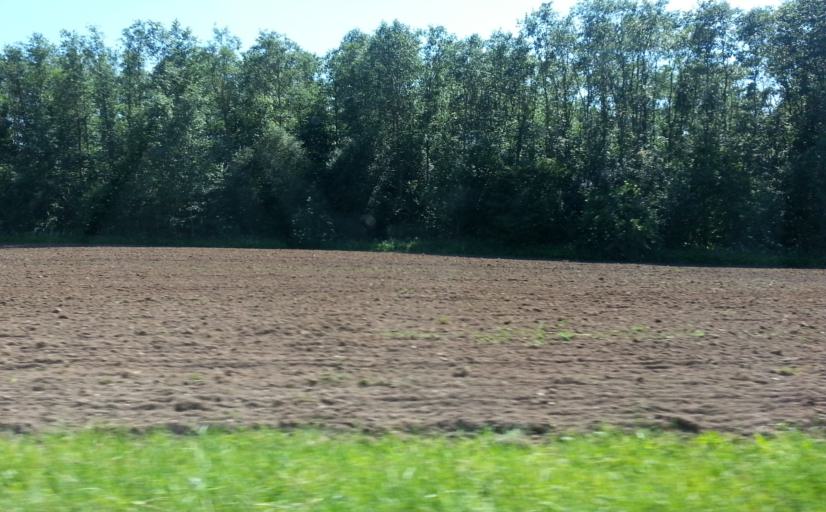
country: LT
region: Panevezys
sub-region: Birzai
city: Birzai
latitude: 56.2111
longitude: 24.6844
